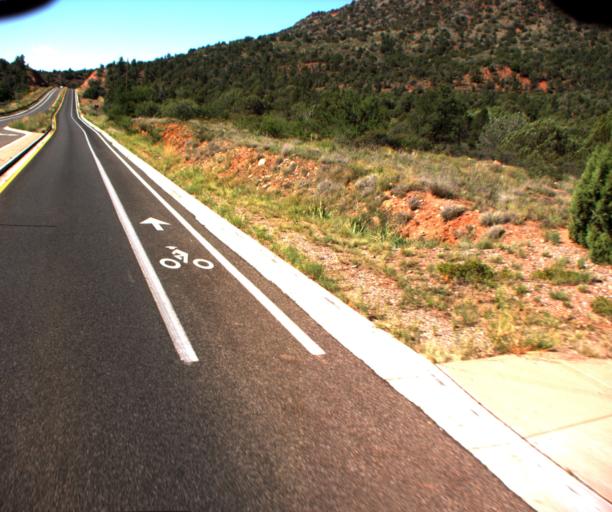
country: US
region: Arizona
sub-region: Yavapai County
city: Big Park
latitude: 34.7674
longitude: -111.7655
